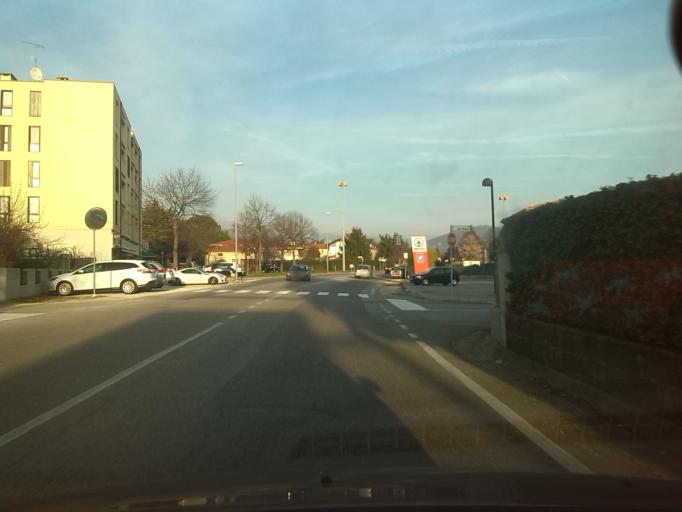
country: IT
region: Friuli Venezia Giulia
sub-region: Provincia di Udine
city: Cividale del Friuli
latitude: 46.0851
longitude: 13.4294
